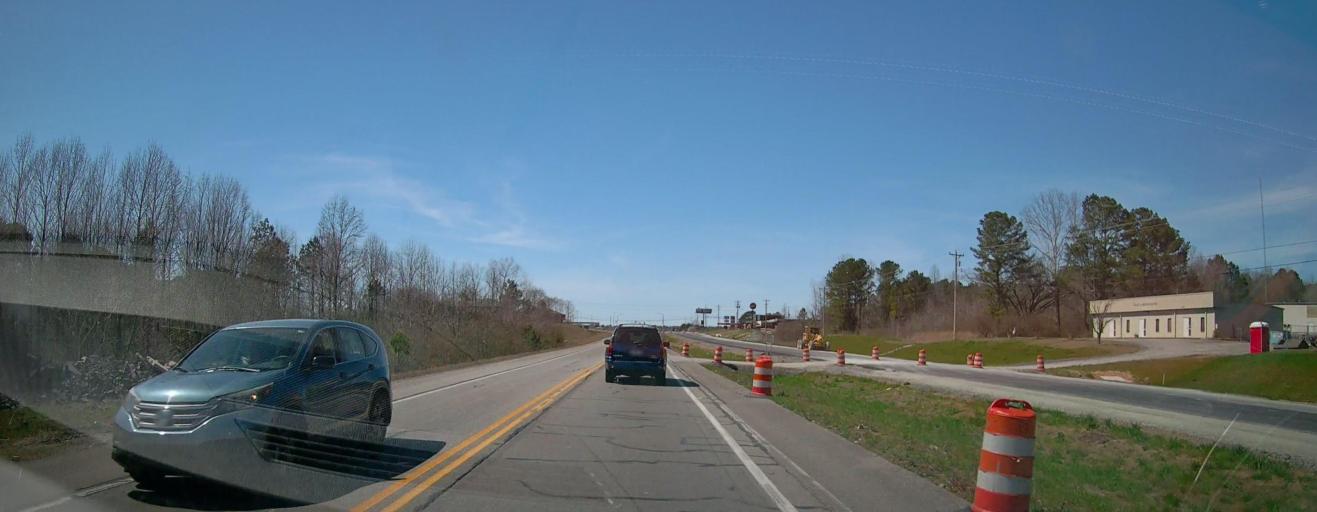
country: US
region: Alabama
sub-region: Cullman County
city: Cullman
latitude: 34.2011
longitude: -86.8224
